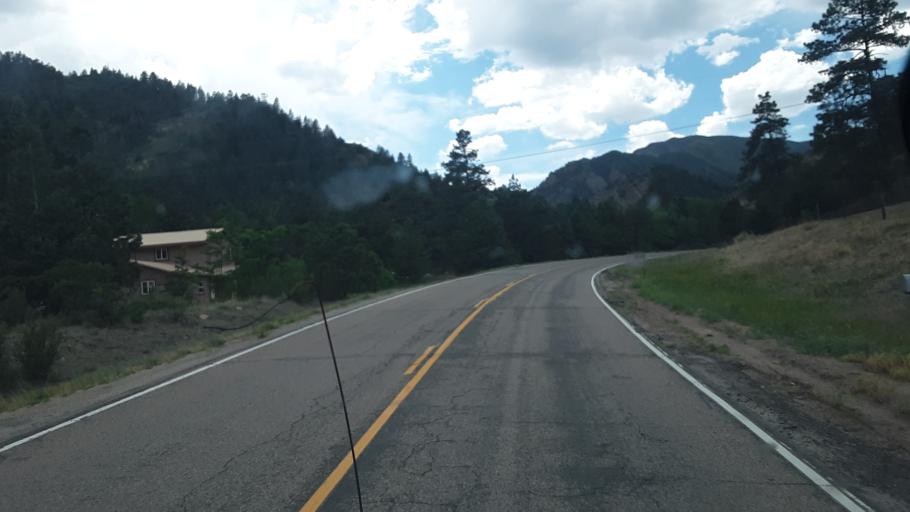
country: US
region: Colorado
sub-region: Fremont County
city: Florence
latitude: 38.1756
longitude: -105.1298
